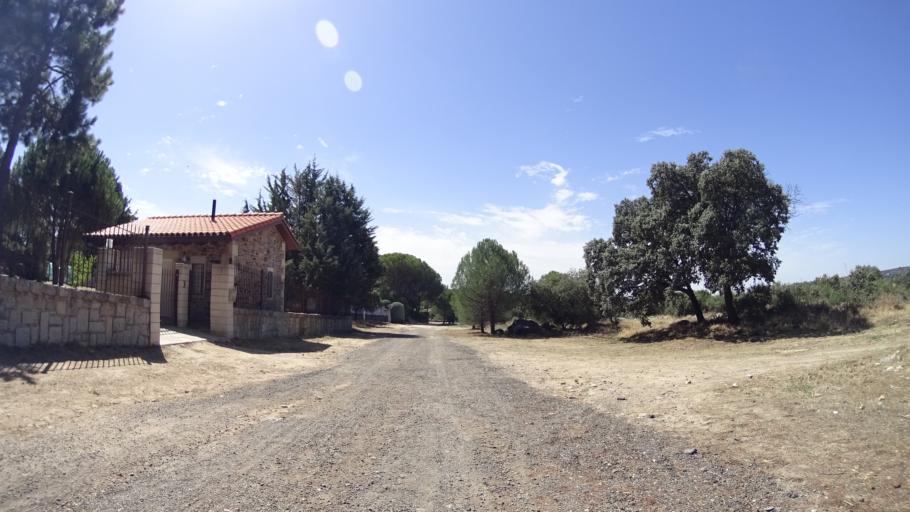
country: ES
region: Madrid
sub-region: Provincia de Madrid
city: Torrelodones
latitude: 40.5708
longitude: -3.9447
